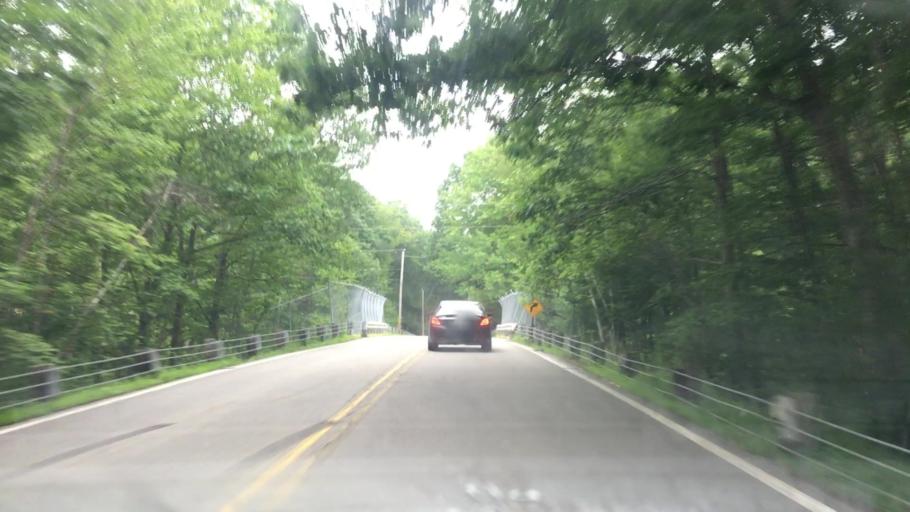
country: US
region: New Hampshire
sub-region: Rockingham County
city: Greenland
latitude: 43.0939
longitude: -70.8417
